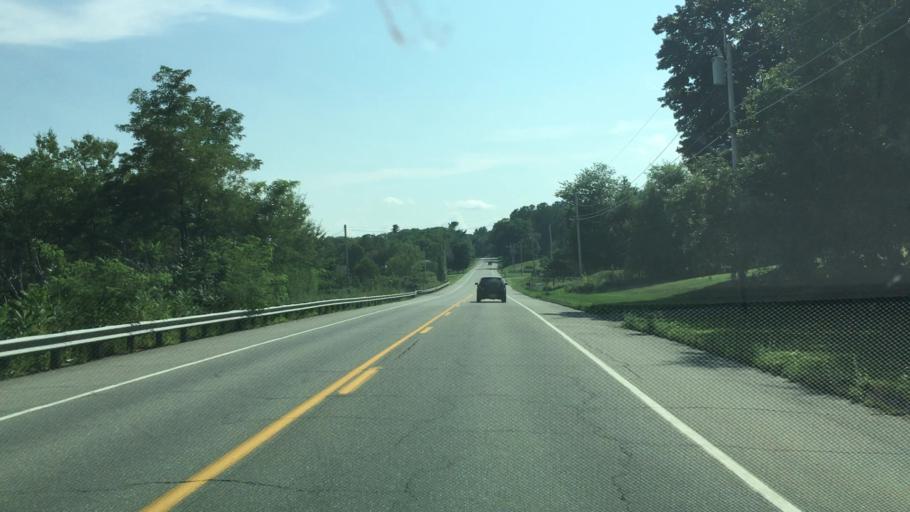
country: US
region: Maine
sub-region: Waldo County
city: Winterport
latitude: 44.6587
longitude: -68.8340
